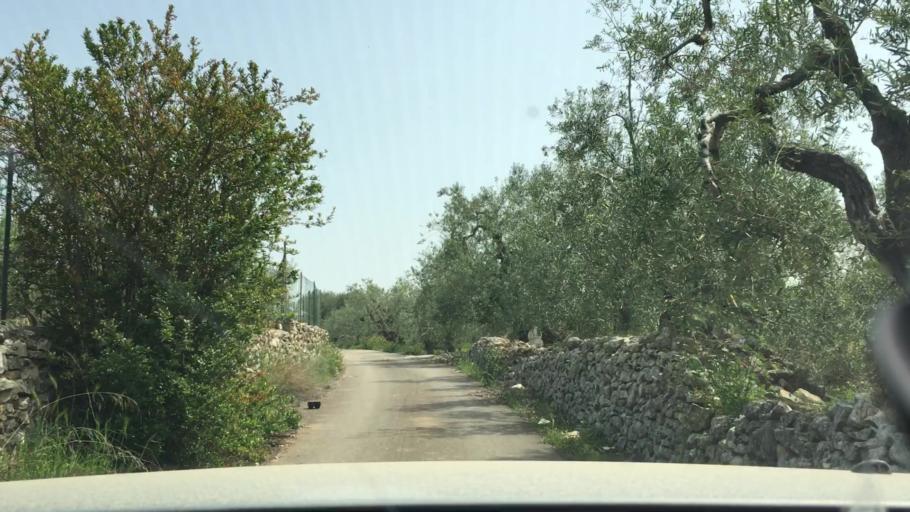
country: IT
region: Apulia
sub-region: Provincia di Barletta - Andria - Trani
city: Capirro
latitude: 41.2559
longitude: 16.4545
